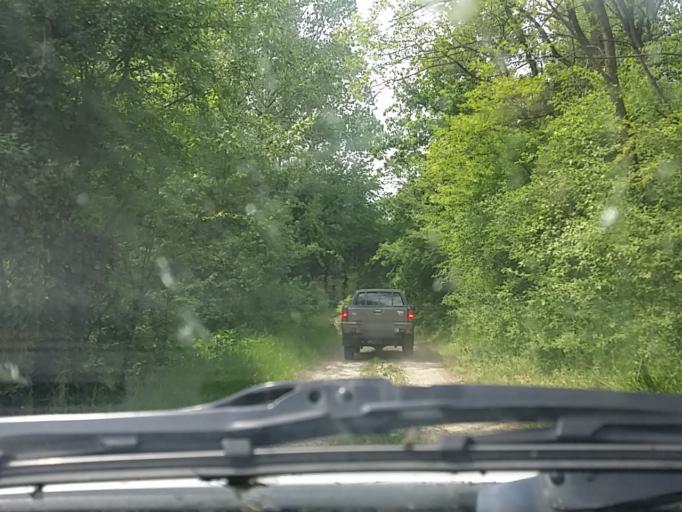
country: HR
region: Koprivnicko-Krizevacka
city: Ferdinandovac
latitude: 46.1055
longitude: 17.2298
